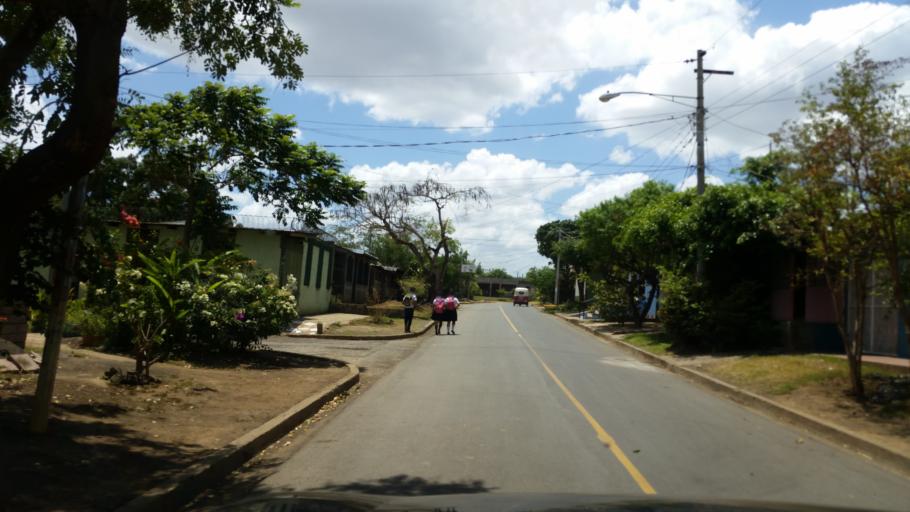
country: NI
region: Managua
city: Managua
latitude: 12.1139
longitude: -86.2078
